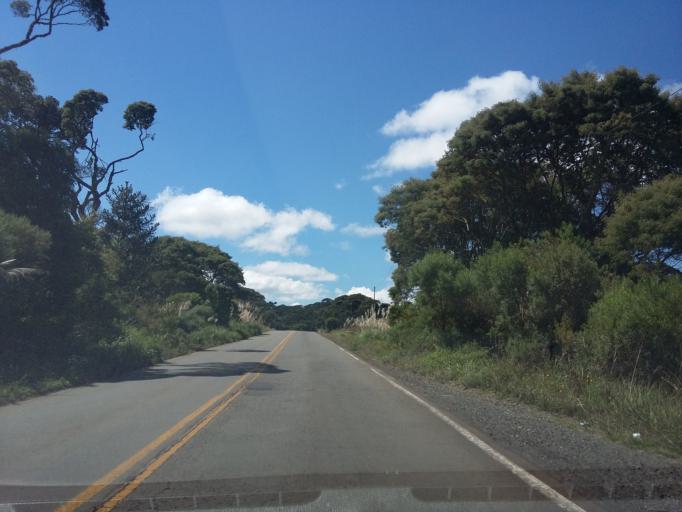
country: BR
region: Santa Catarina
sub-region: Sao Joaquim
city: Sao Joaquim
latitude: -28.2846
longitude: -49.7512
